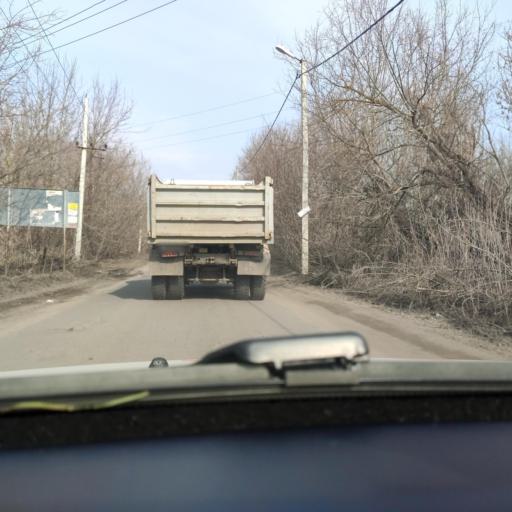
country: RU
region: Voronezj
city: Ramon'
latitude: 51.9064
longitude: 39.3634
